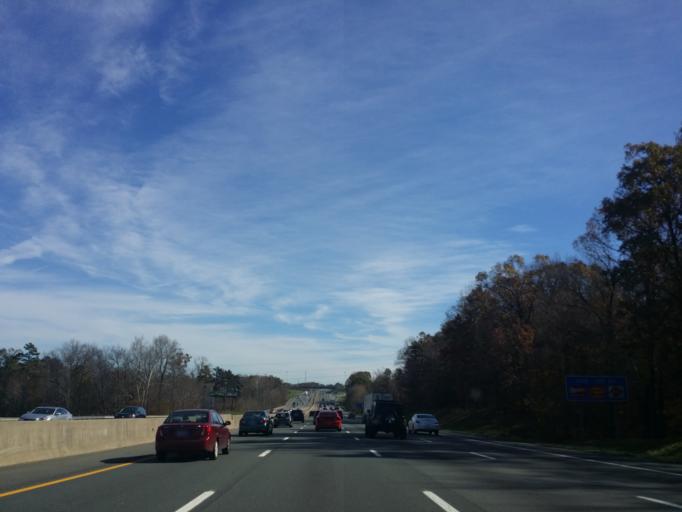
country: US
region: North Carolina
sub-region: Alamance County
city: Haw River
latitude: 36.0687
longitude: -79.3655
